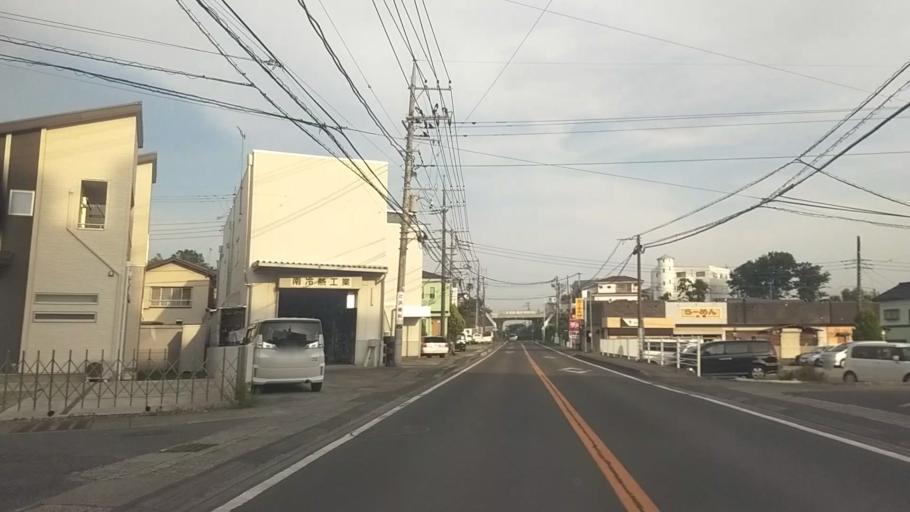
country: JP
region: Kanagawa
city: Odawara
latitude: 35.3134
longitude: 139.1163
